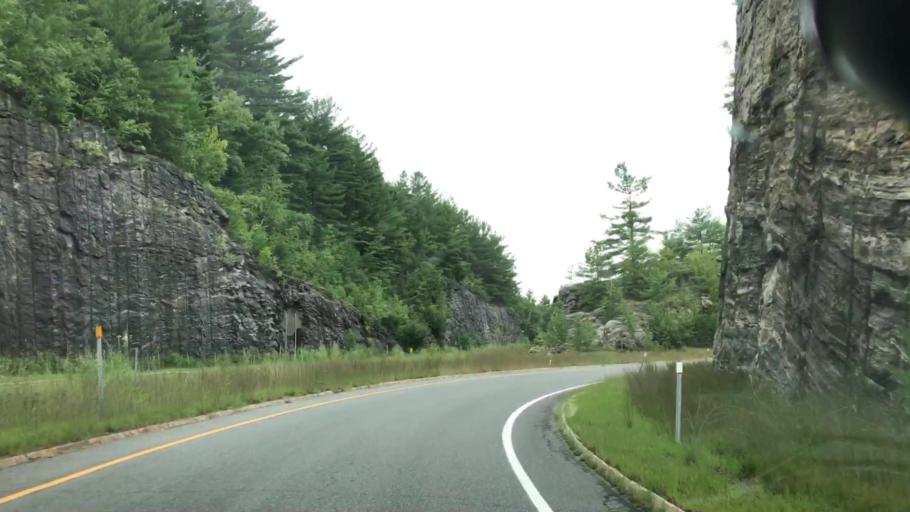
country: US
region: New Hampshire
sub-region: Hillsborough County
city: Milford
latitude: 42.8220
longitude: -71.6174
